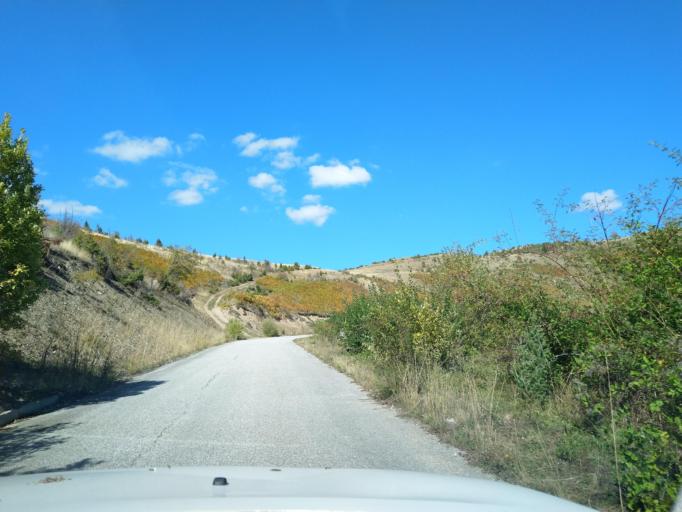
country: RS
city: Sokolovica
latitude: 43.2532
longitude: 20.3324
